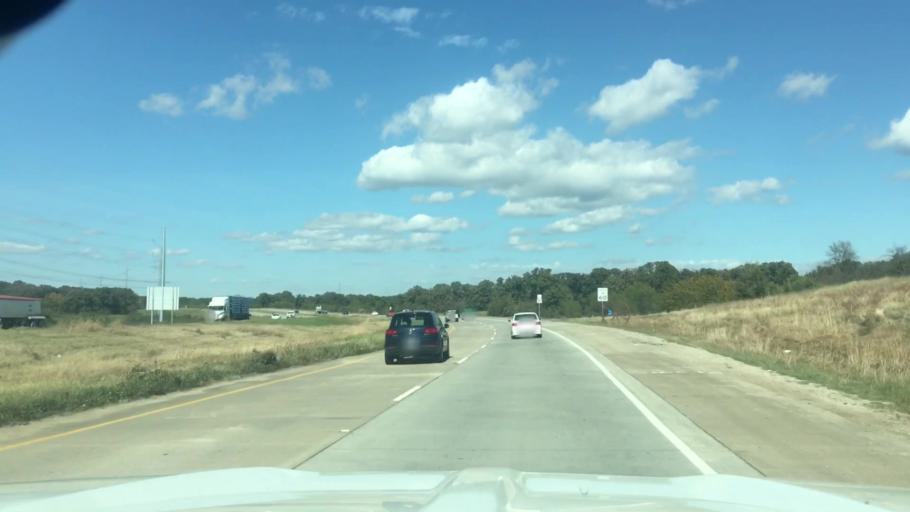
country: US
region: Texas
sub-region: Denton County
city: Denton
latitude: 33.2397
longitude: -97.0895
